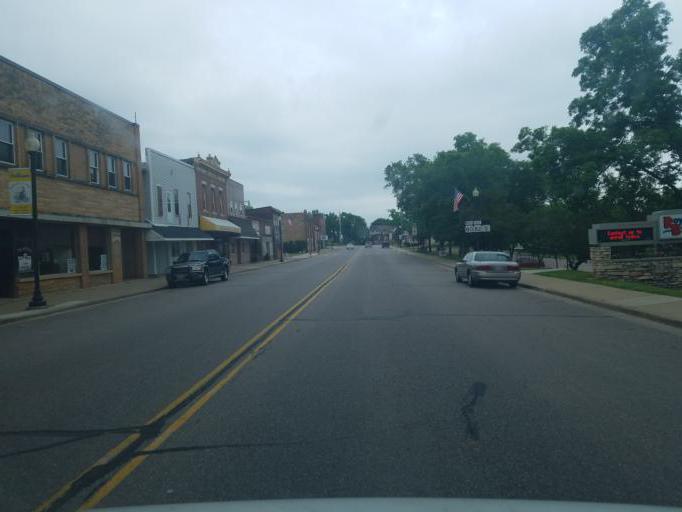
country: US
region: Wisconsin
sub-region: Juneau County
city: Elroy
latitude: 43.7385
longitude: -90.2703
